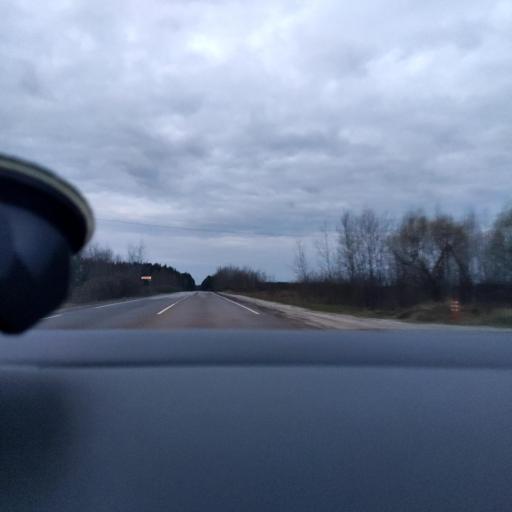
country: RU
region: Moskovskaya
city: Krasnyy Tkach
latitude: 55.4224
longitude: 39.1867
